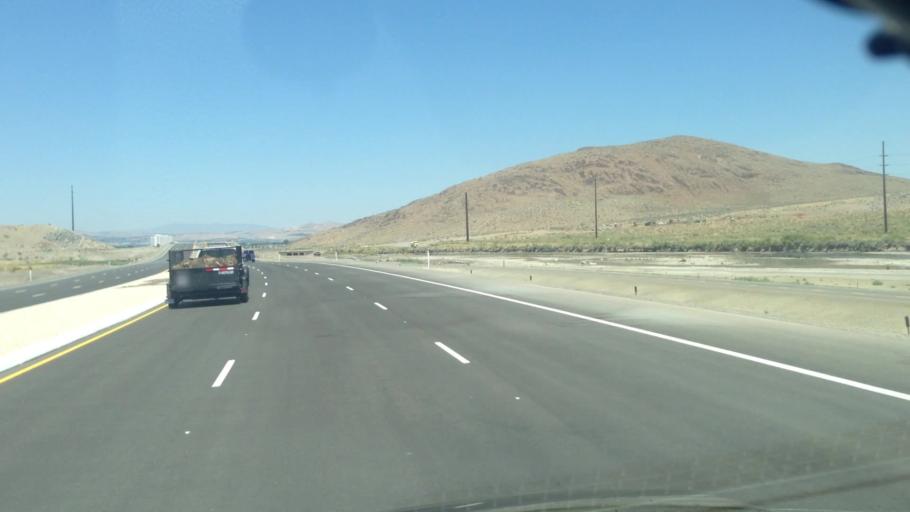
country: US
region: Nevada
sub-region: Washoe County
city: Sparks
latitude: 39.4615
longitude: -119.7259
